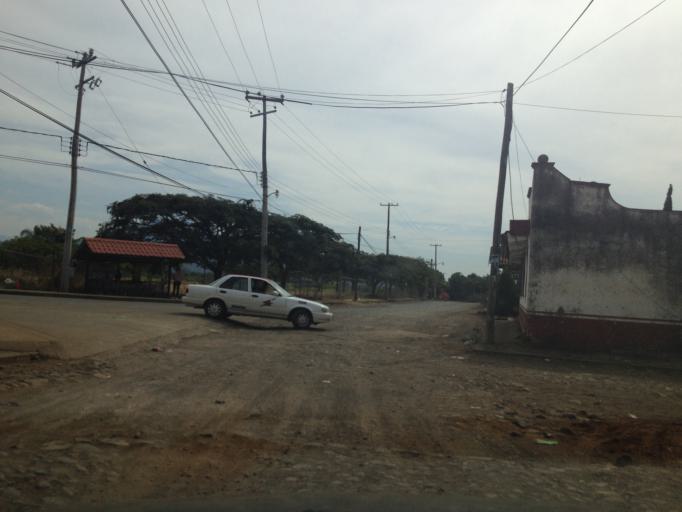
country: MX
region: Michoacan
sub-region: Ziracuaretiro
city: Patuan
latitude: 19.4317
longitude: -101.9245
